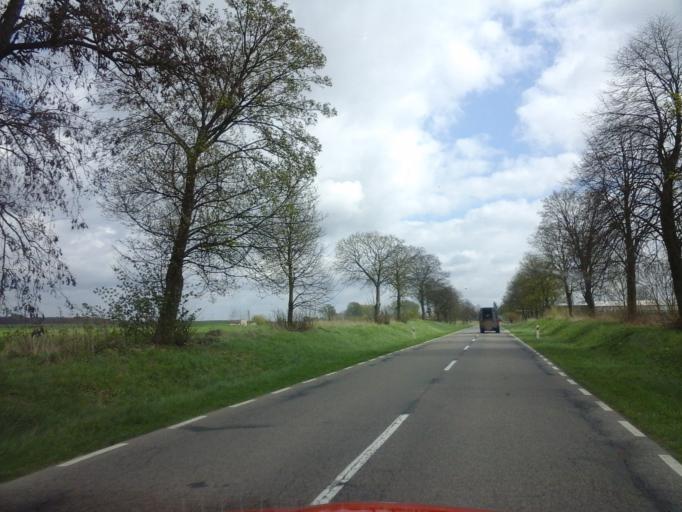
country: PL
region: West Pomeranian Voivodeship
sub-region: Powiat choszczenski
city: Krzecin
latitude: 53.1216
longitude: 15.5623
